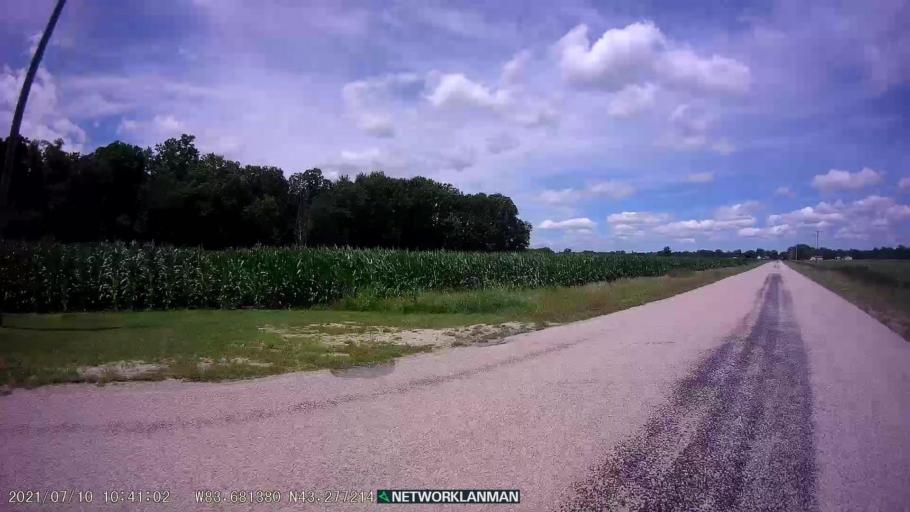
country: US
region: Michigan
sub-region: Saginaw County
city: Frankenmuth
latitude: 43.2772
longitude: -83.6813
